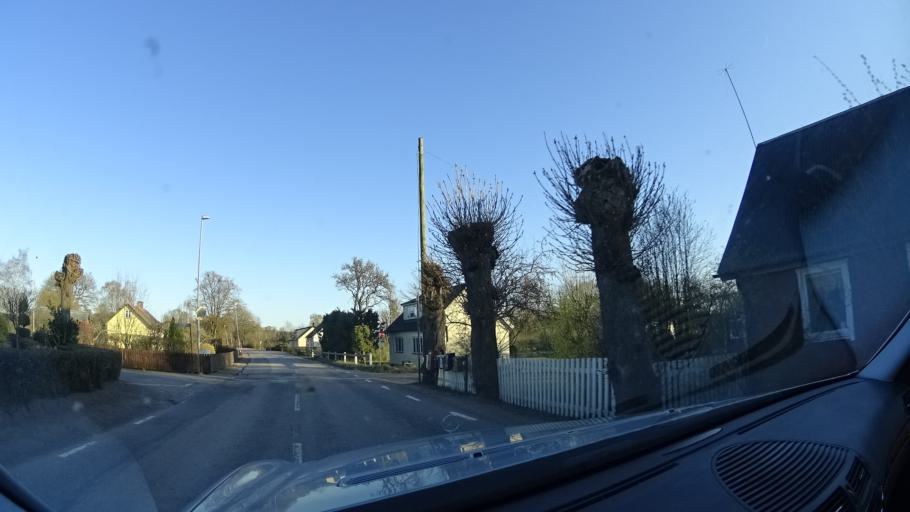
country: SE
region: Skane
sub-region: Bjuvs Kommun
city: Billesholm
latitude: 56.0476
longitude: 13.0020
